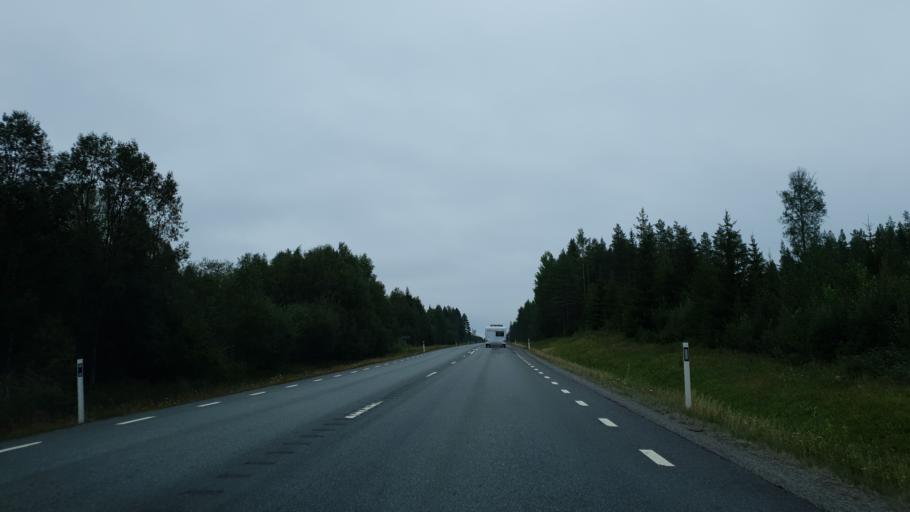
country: SE
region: Vaesterbotten
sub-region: Skelleftea Kommun
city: Burea
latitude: 64.3409
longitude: 21.2788
